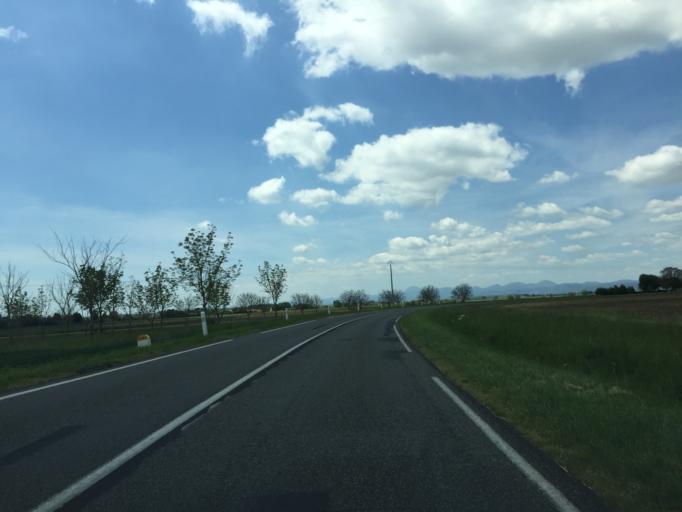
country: FR
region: Auvergne
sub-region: Departement du Puy-de-Dome
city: Aigueperse
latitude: 46.0273
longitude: 3.2478
